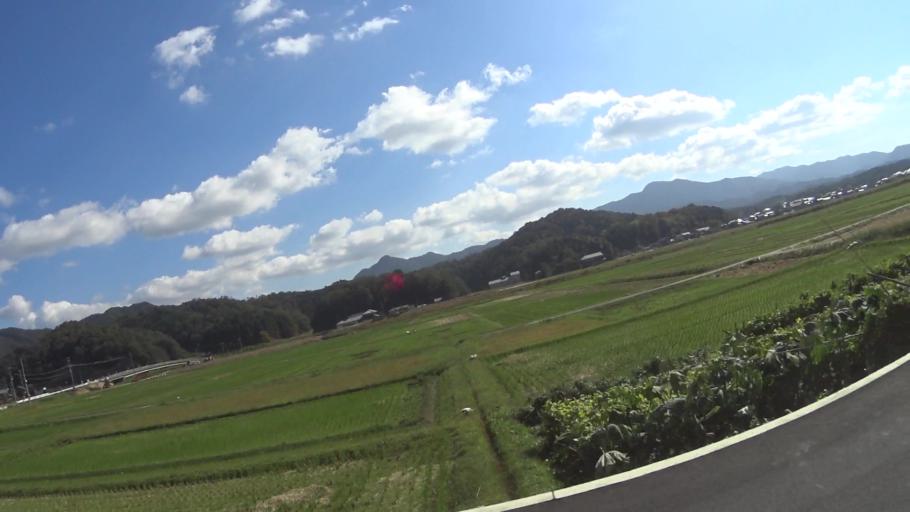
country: JP
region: Kyoto
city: Miyazu
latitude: 35.6884
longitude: 135.0938
